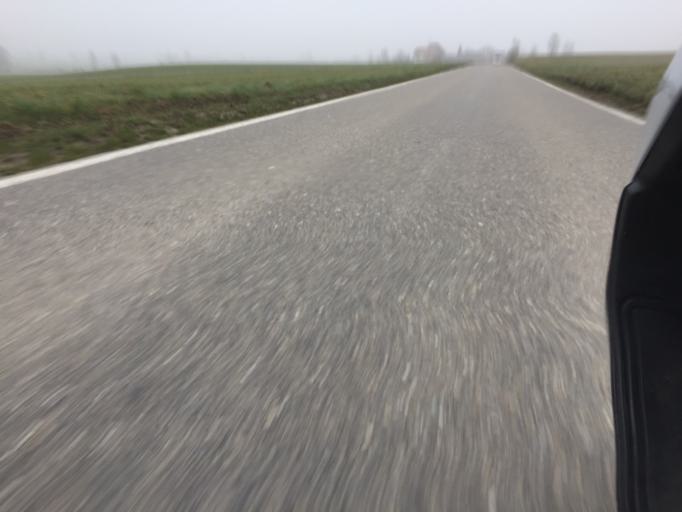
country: CH
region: Bern
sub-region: Seeland District
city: Grossaffoltern
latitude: 47.0835
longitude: 7.3838
